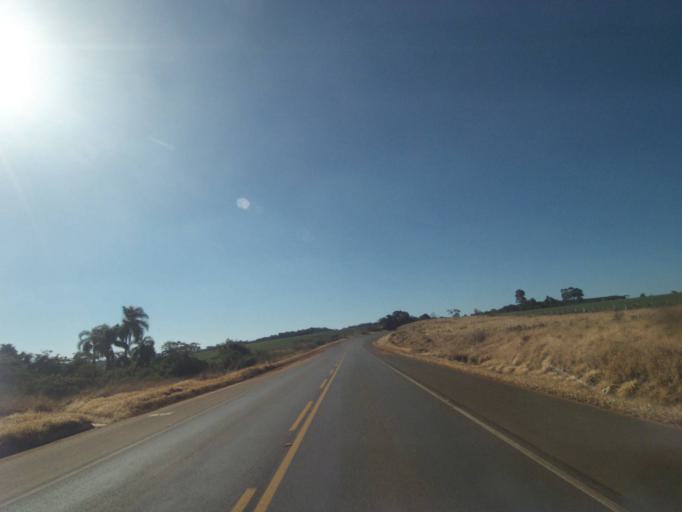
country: BR
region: Parana
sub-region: Tibagi
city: Tibagi
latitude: -24.7418
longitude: -50.4598
